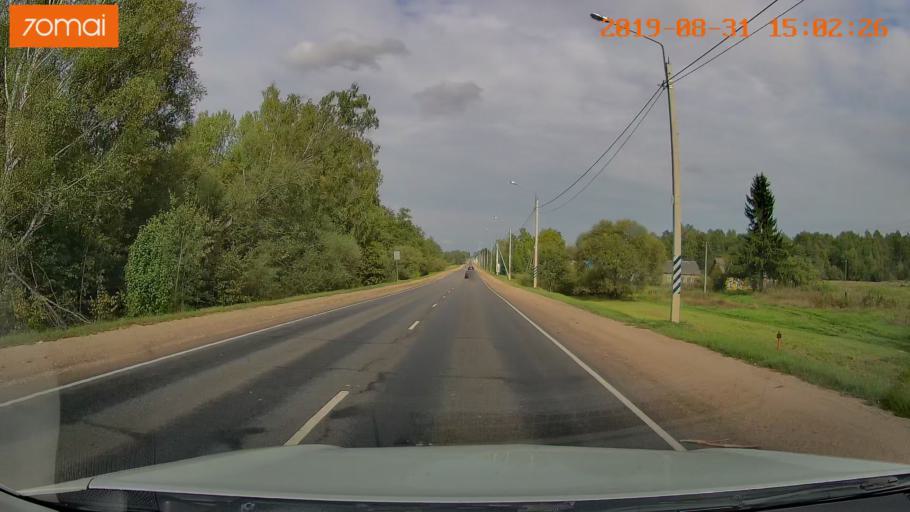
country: RU
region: Kaluga
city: Spas-Demensk
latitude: 54.3456
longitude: 34.0743
